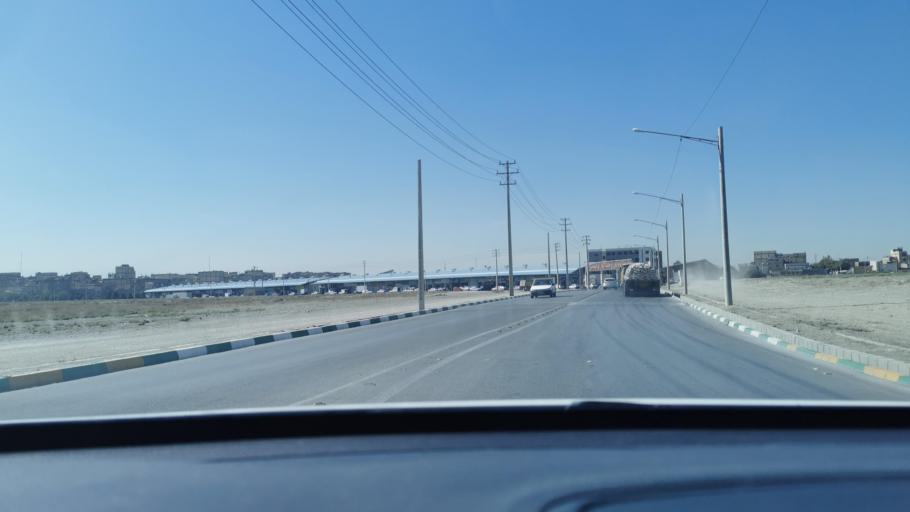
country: IR
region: Razavi Khorasan
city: Mashhad
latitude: 36.3360
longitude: 59.6222
